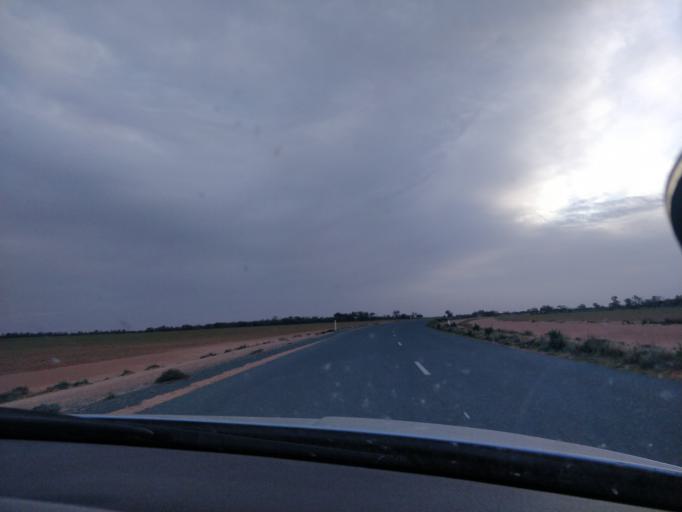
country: AU
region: New South Wales
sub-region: Wentworth
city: Gol Gol
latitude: -34.0363
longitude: 142.3686
